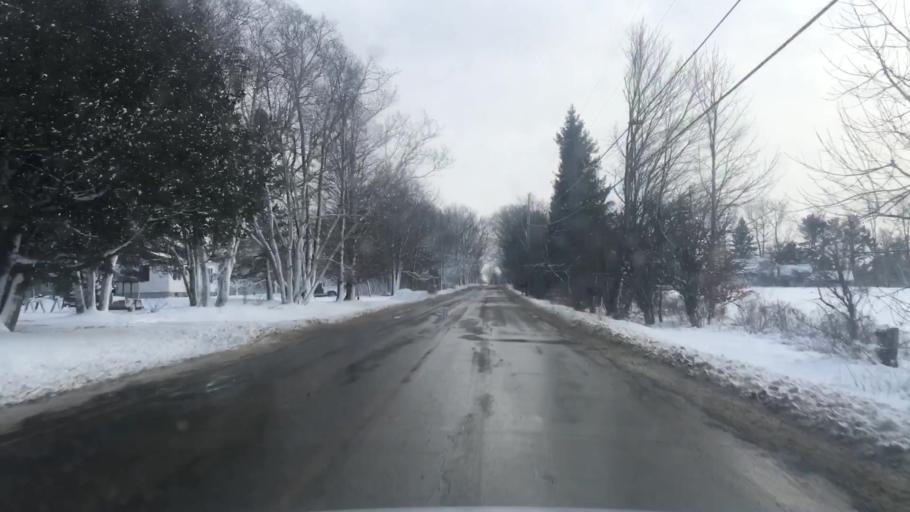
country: US
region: Maine
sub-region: Waldo County
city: Palermo
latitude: 44.3595
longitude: -69.4534
